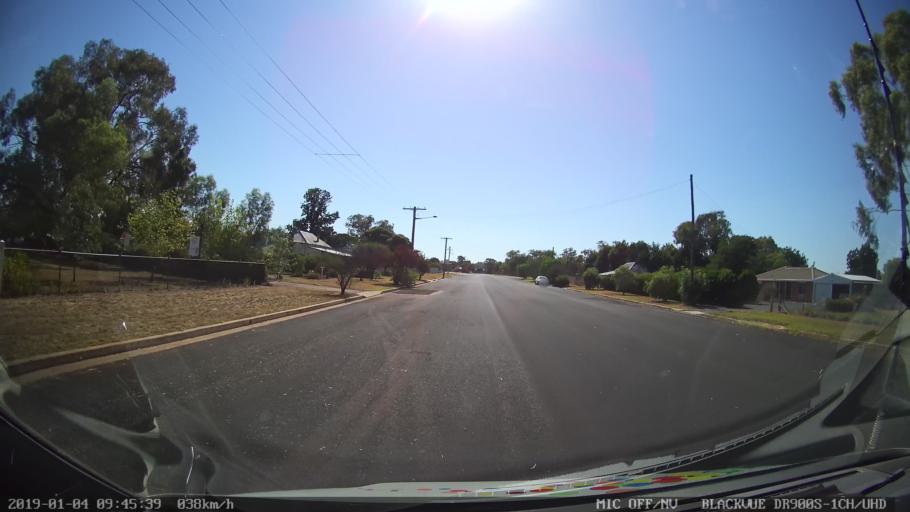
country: AU
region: New South Wales
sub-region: Cabonne
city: Canowindra
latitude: -33.6161
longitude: 148.4330
